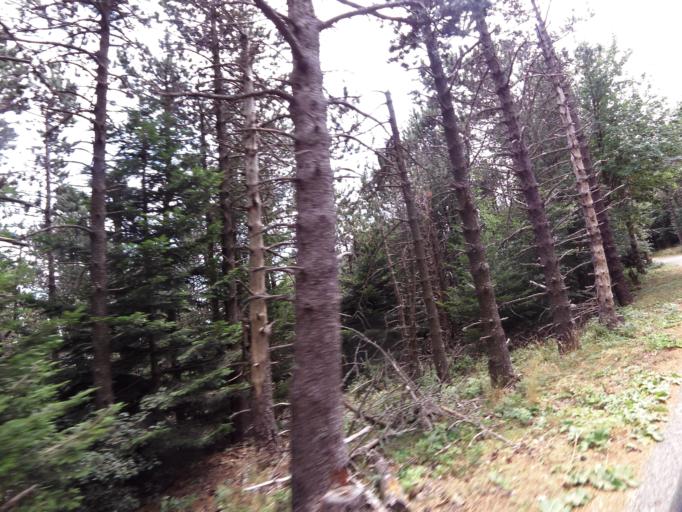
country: FR
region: Languedoc-Roussillon
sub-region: Departement du Gard
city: Valleraugue
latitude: 44.0630
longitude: 3.6048
